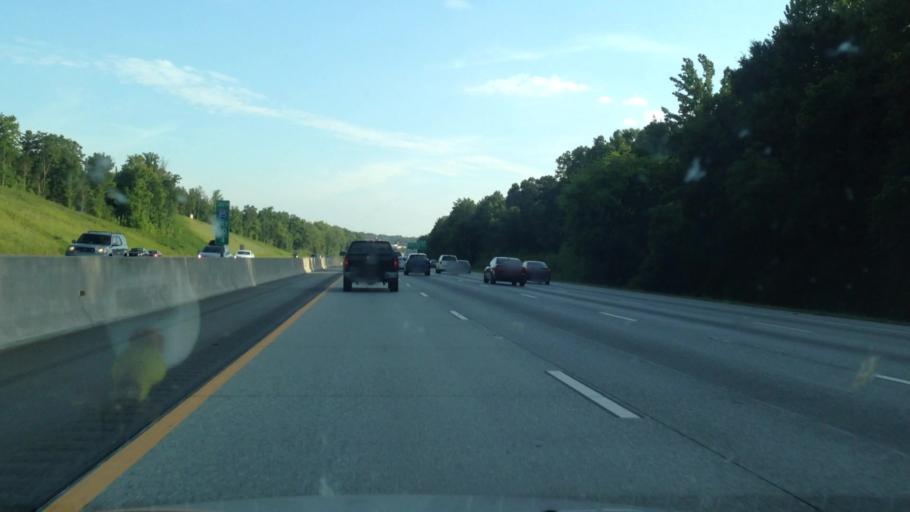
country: US
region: North Carolina
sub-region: Cabarrus County
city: Harrisburg
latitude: 35.3826
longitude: -80.7056
